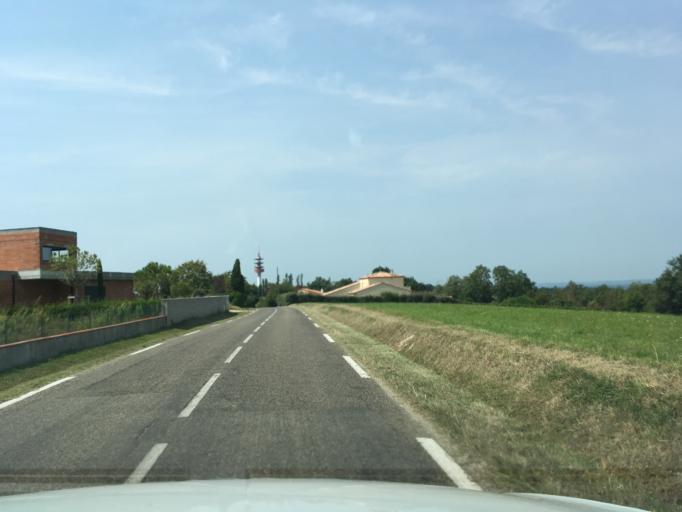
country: FR
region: Midi-Pyrenees
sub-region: Departement du Tarn-et-Garonne
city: Corbarieu
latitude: 43.9639
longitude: 1.3858
